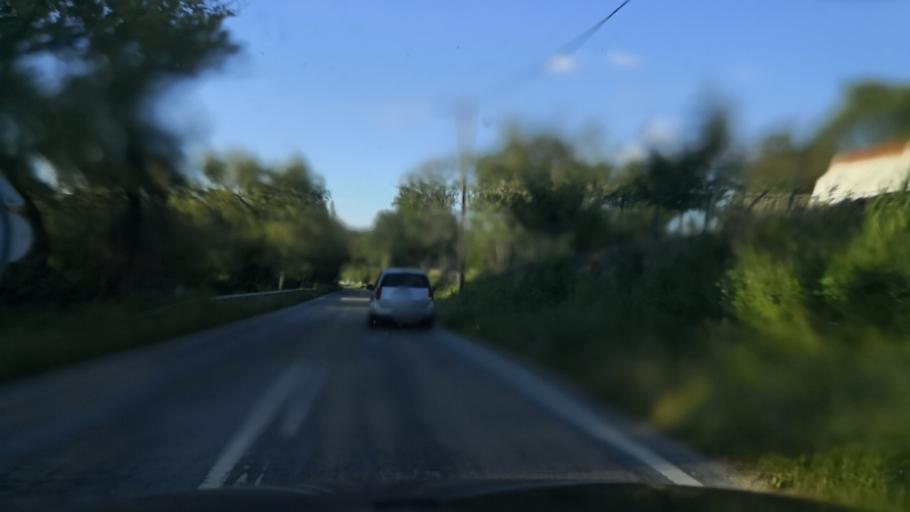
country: PT
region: Portalegre
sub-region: Portalegre
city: Reguengo
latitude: 39.3473
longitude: -7.4068
